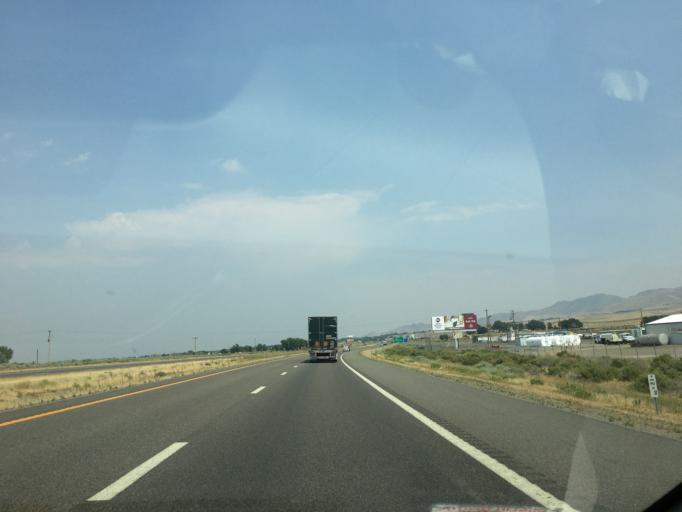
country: US
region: Nevada
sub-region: Humboldt County
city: Winnemucca
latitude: 40.9415
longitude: -117.7787
